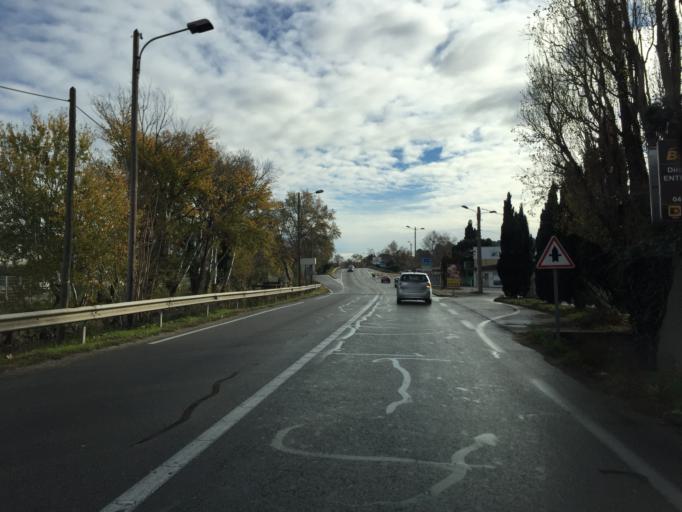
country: FR
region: Provence-Alpes-Cote d'Azur
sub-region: Departement du Vaucluse
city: Vedene
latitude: 43.9891
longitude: 4.8930
